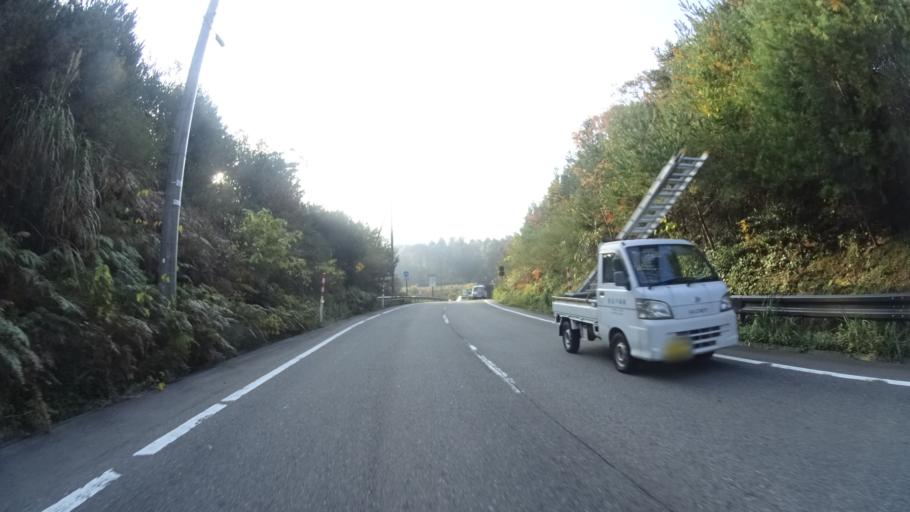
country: JP
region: Ishikawa
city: Nanao
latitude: 37.0234
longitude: 136.9853
